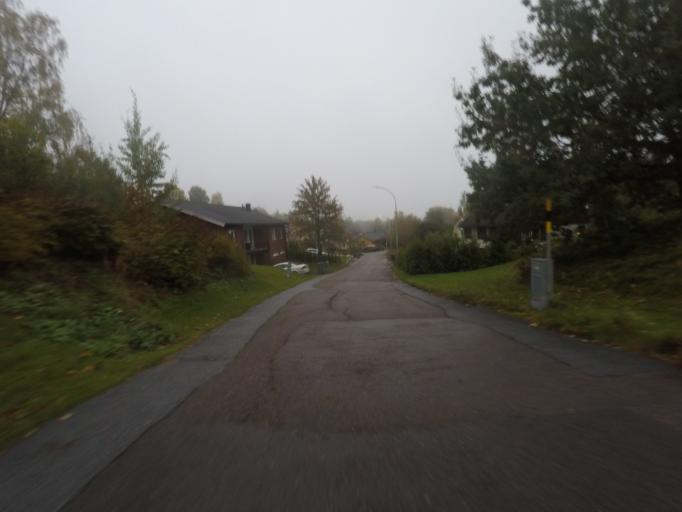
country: SE
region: OErebro
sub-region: Karlskoga Kommun
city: Karlskoga
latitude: 59.3123
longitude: 14.5088
